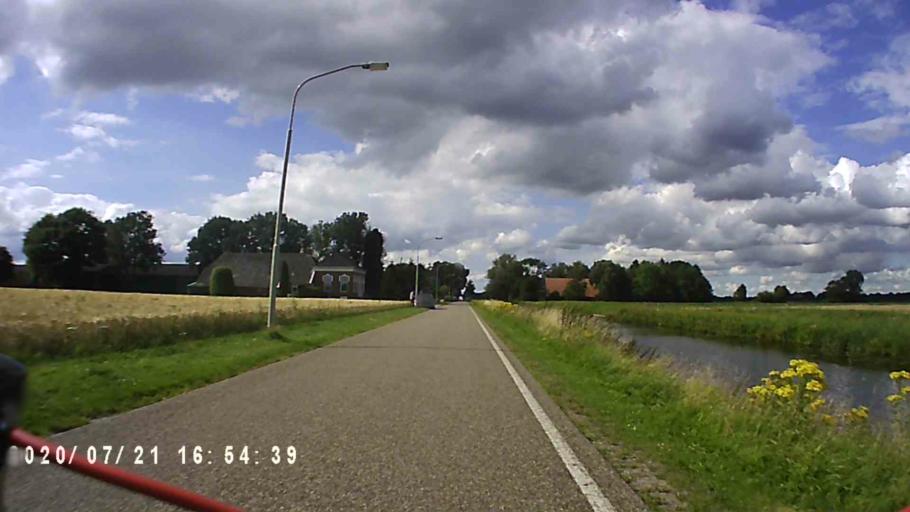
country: NL
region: Groningen
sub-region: Gemeente Hoogezand-Sappemeer
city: Hoogezand
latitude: 53.1289
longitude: 6.7671
